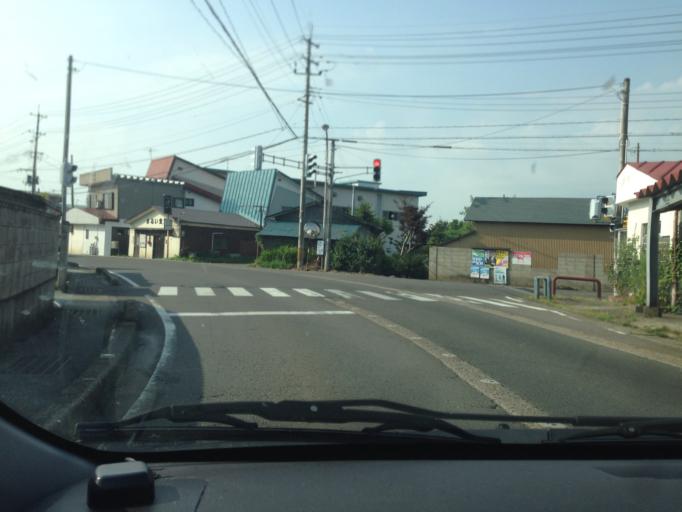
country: JP
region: Fukushima
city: Kitakata
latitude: 37.6778
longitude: 139.8698
